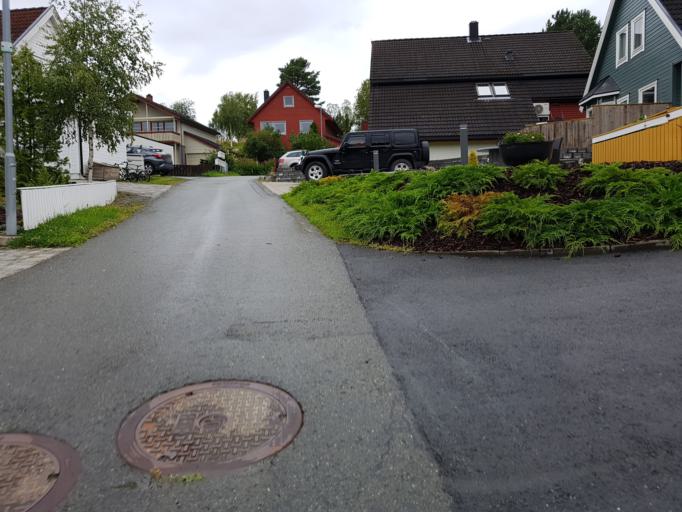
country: NO
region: Sor-Trondelag
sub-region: Trondheim
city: Trondheim
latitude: 63.4086
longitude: 10.4859
